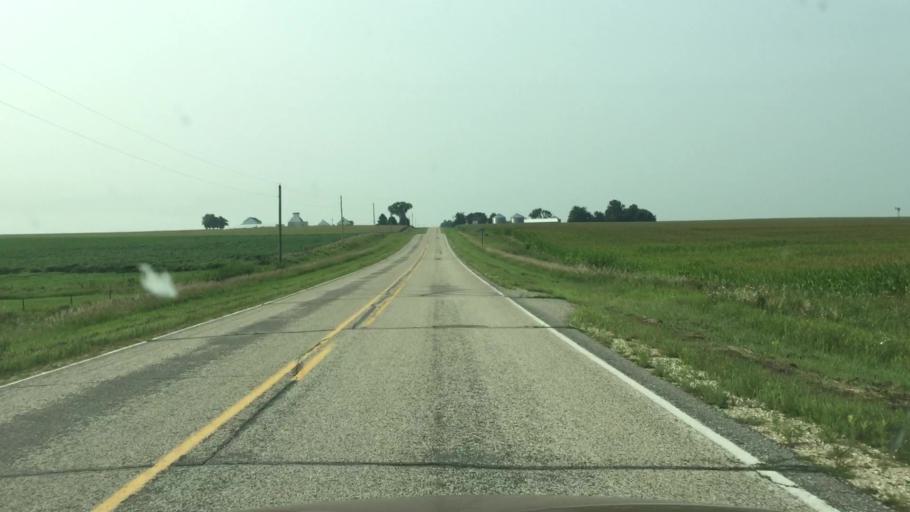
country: US
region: Iowa
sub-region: O'Brien County
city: Sheldon
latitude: 43.2755
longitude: -95.7829
